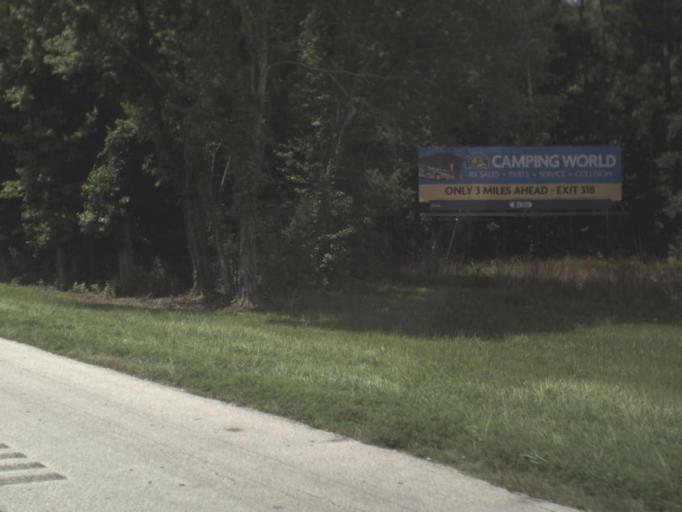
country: US
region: Florida
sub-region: Saint Johns County
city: Villano Beach
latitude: 29.9664
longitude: -81.4501
